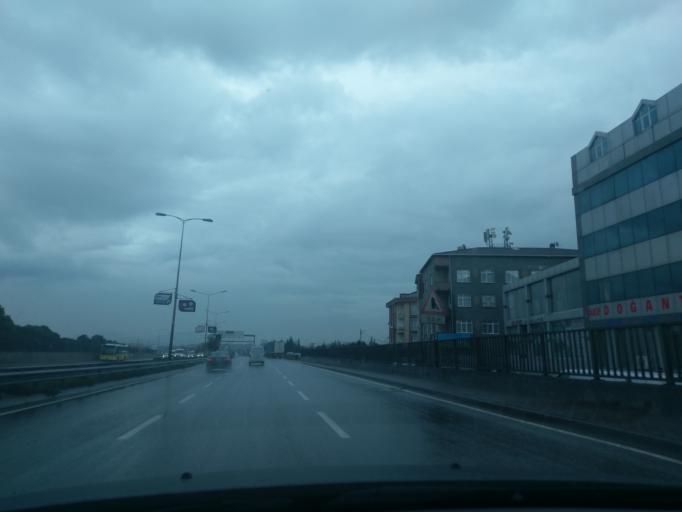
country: TR
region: Istanbul
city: Samandira
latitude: 41.0140
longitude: 29.1987
